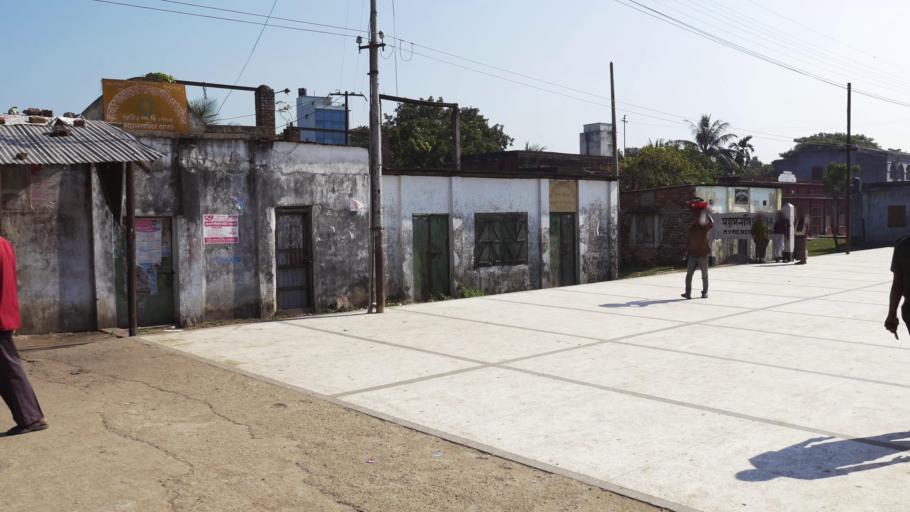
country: BD
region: Dhaka
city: Mymensingh
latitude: 24.6960
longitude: 90.4520
